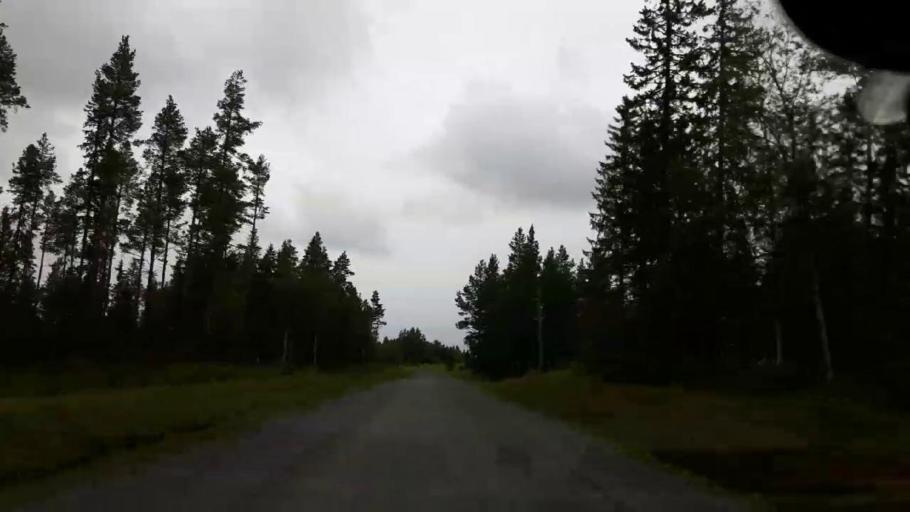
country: SE
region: Jaemtland
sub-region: OEstersunds Kommun
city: Ostersund
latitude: 63.0854
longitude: 14.5553
